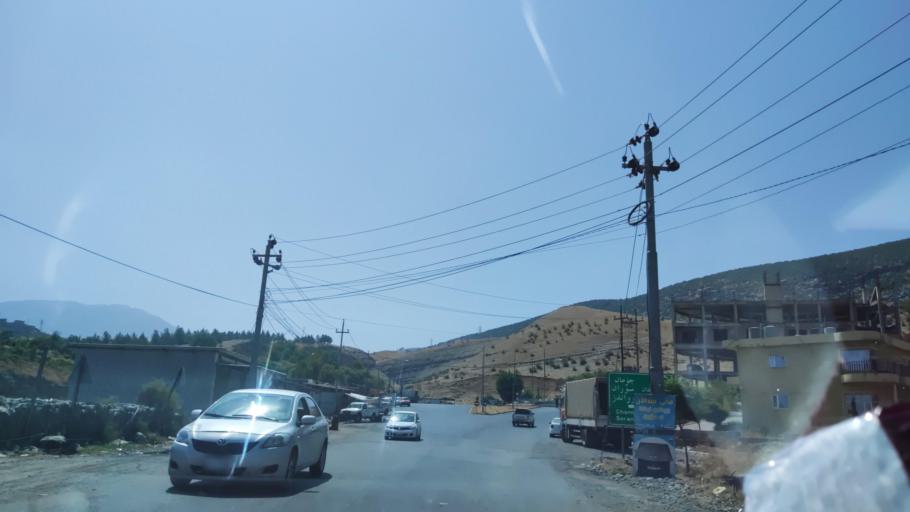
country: IQ
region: Arbil
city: Ruwandiz
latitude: 36.6493
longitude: 44.4985
